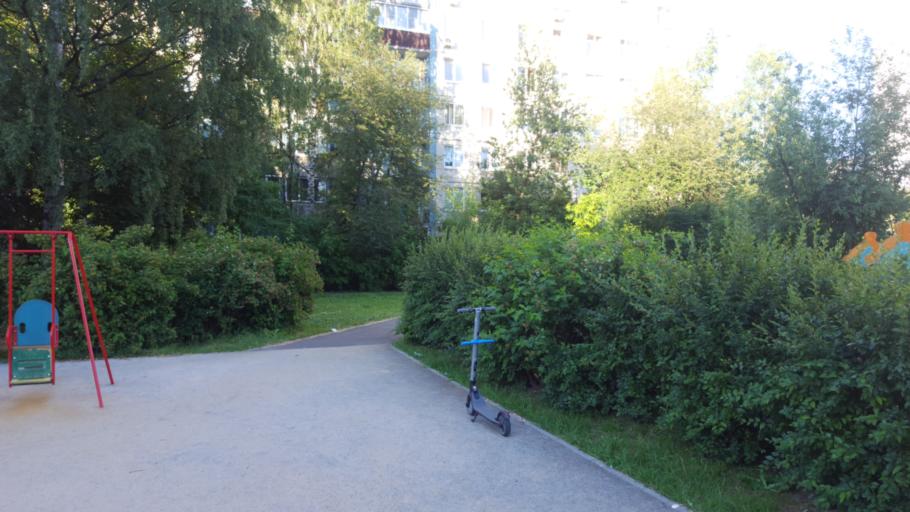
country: RU
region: St.-Petersburg
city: Krasnogvargeisky
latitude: 59.9151
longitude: 30.4927
